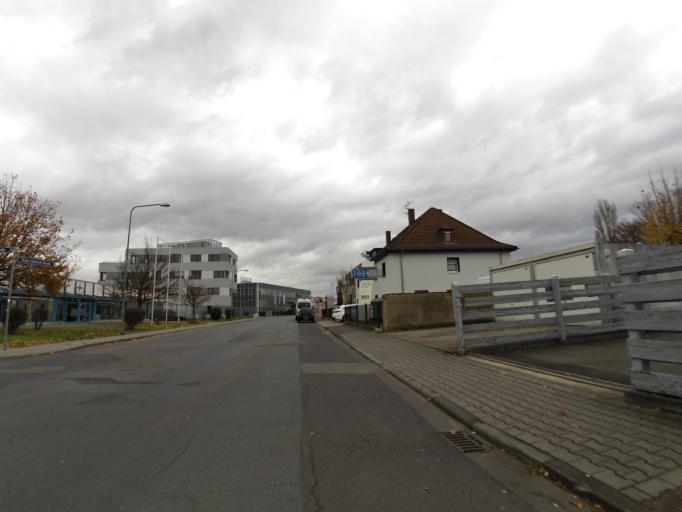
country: DE
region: Hesse
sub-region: Regierungsbezirk Darmstadt
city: Bad Vilbel
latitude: 50.1431
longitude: 8.7443
